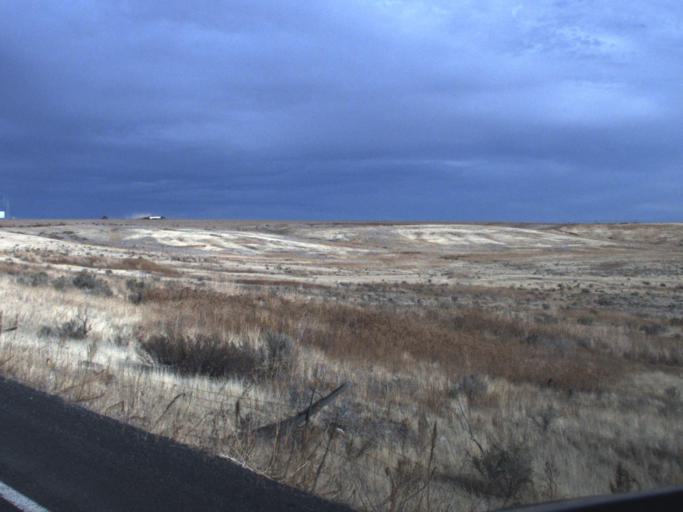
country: US
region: Washington
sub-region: Adams County
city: Ritzville
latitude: 47.3517
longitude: -118.6965
